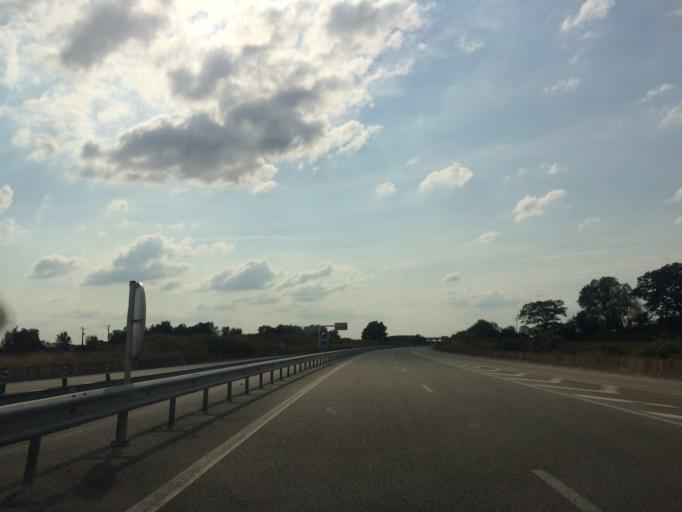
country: FR
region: Lower Normandy
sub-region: Departement de l'Orne
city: Valframbert
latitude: 48.4796
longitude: 0.2447
